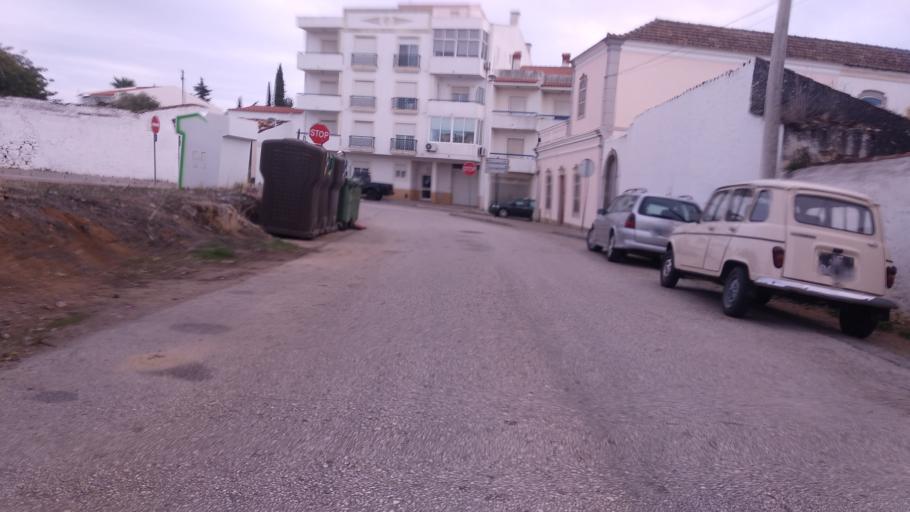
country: PT
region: Faro
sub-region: Sao Bras de Alportel
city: Sao Bras de Alportel
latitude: 37.1520
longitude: -7.8914
